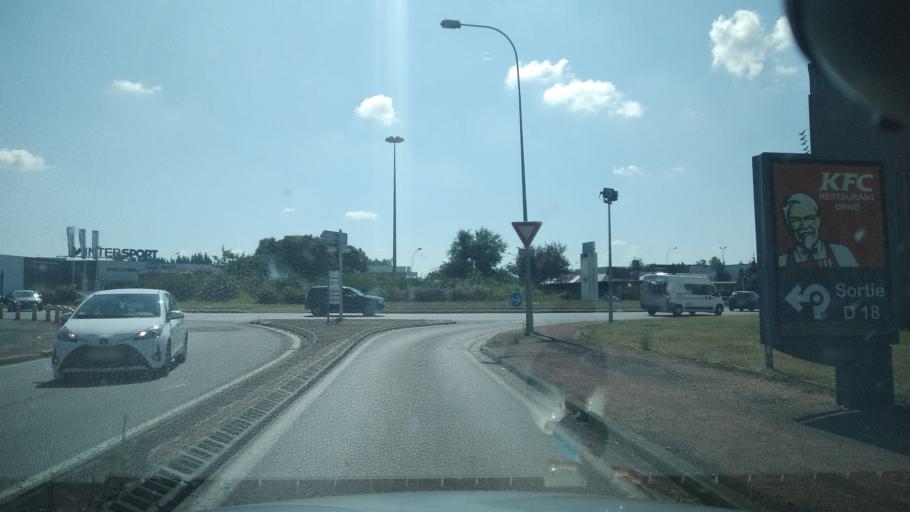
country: FR
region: Poitou-Charentes
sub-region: Departement de la Vienne
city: Chasseneuil-du-Poitou
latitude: 46.6471
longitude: 0.3615
